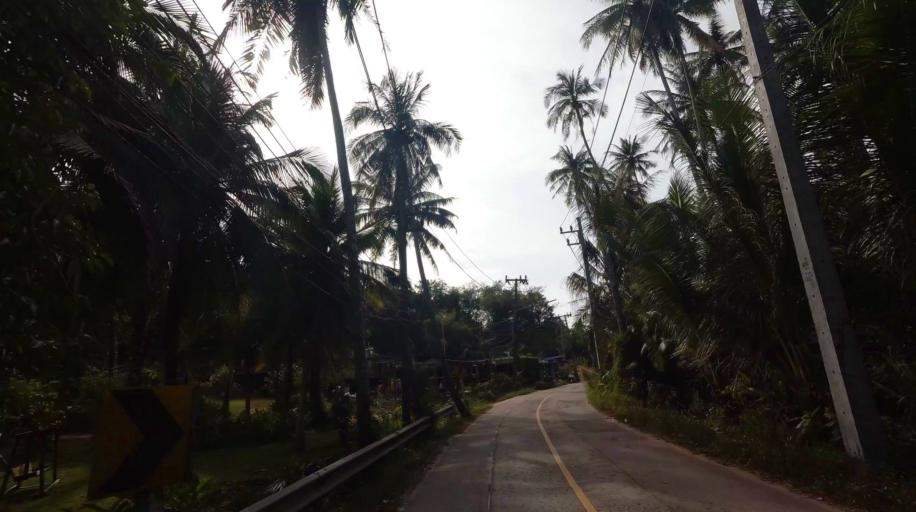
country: TH
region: Trat
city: Ko Kut
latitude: 11.6205
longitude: 102.5459
